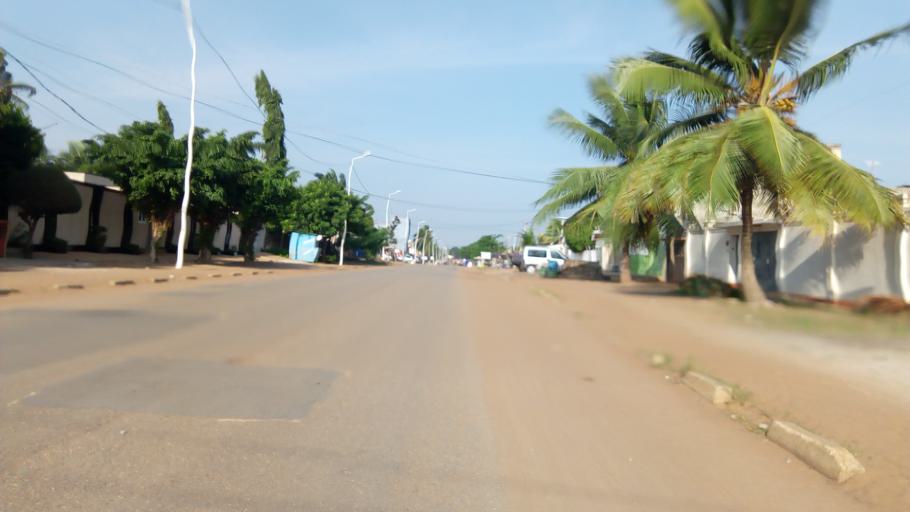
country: TG
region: Maritime
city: Lome
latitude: 6.1813
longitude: 1.1894
